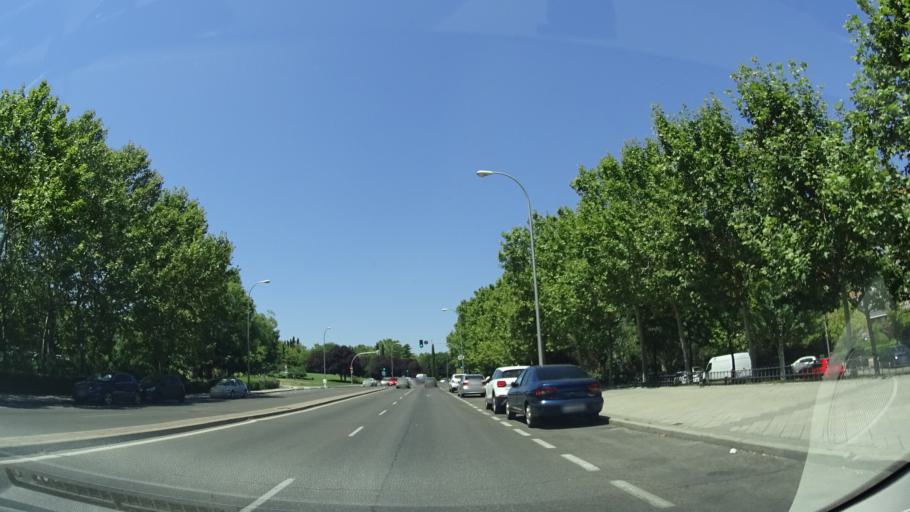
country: ES
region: Madrid
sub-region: Provincia de Madrid
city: Latina
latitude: 40.3769
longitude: -3.7523
